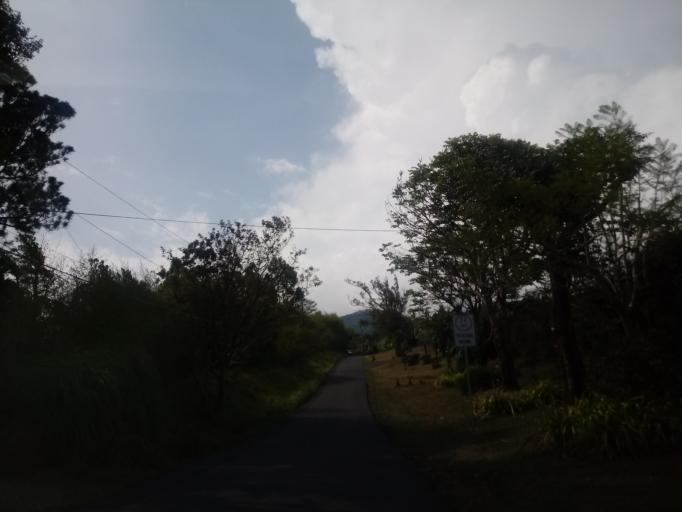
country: CR
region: Heredia
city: Angeles
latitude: 10.0291
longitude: -84.0442
